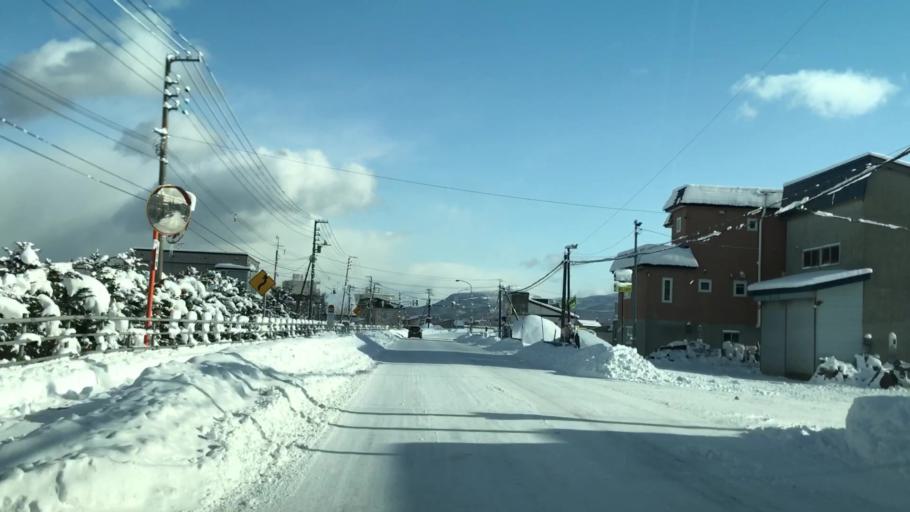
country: JP
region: Hokkaido
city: Yoichi
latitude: 43.2099
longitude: 140.7620
